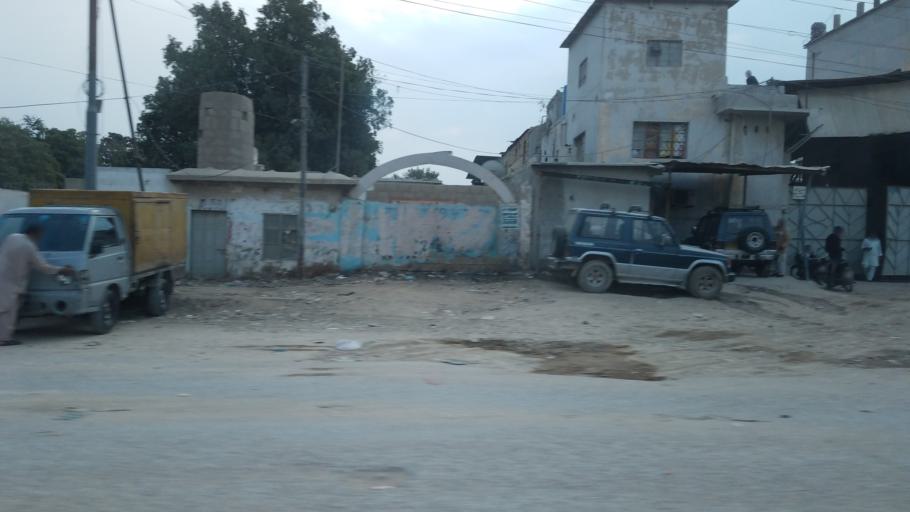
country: PK
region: Sindh
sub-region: Karachi District
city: Karachi
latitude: 24.9407
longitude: 67.0851
